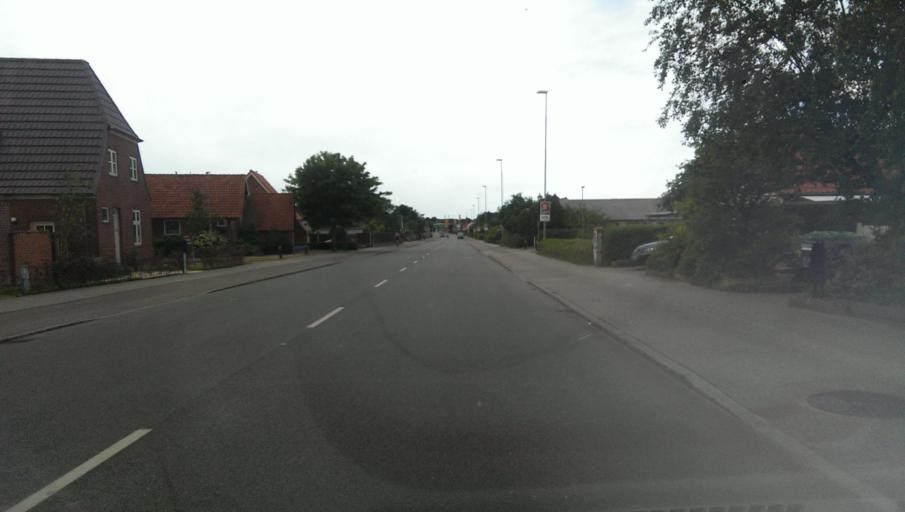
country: DK
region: South Denmark
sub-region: Esbjerg Kommune
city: Esbjerg
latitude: 55.4796
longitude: 8.4739
